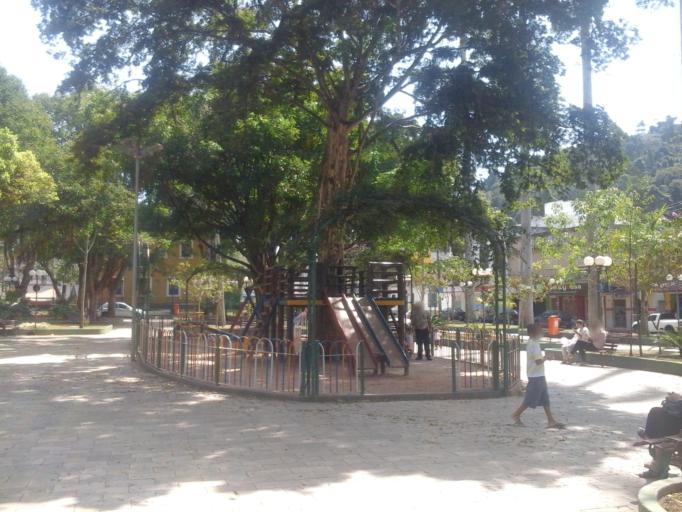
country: BR
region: Rio de Janeiro
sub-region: Pirai
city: Pirai
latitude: -22.6290
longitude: -43.8976
